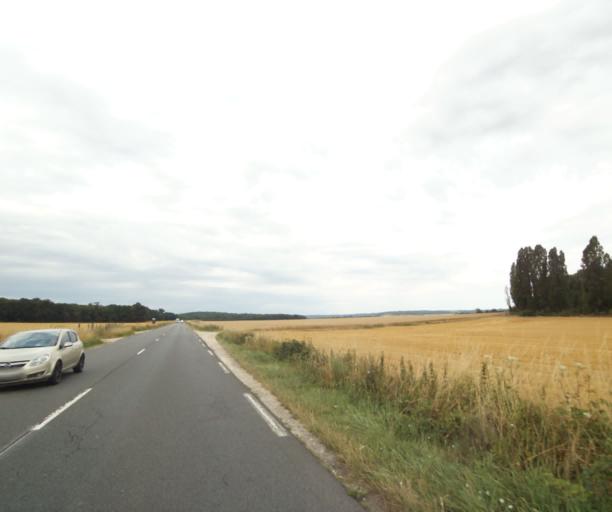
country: FR
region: Ile-de-France
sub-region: Departement de Seine-et-Marne
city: Cely
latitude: 48.4544
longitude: 2.5149
